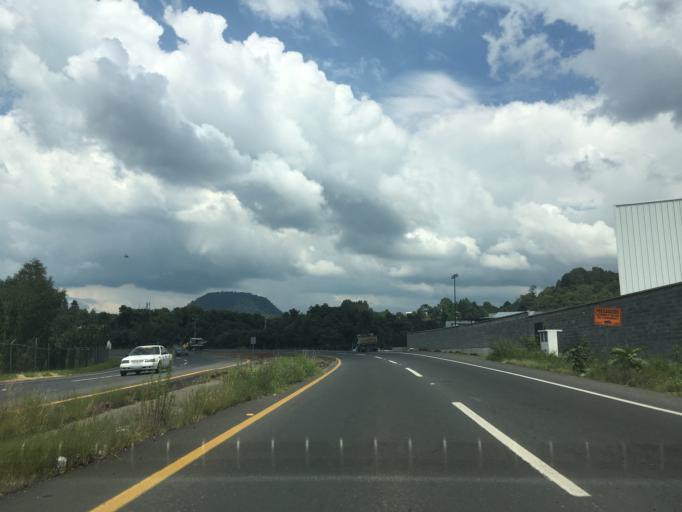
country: MX
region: Michoacan
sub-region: Uruapan
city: Uruapan
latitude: 19.4392
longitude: -102.0709
